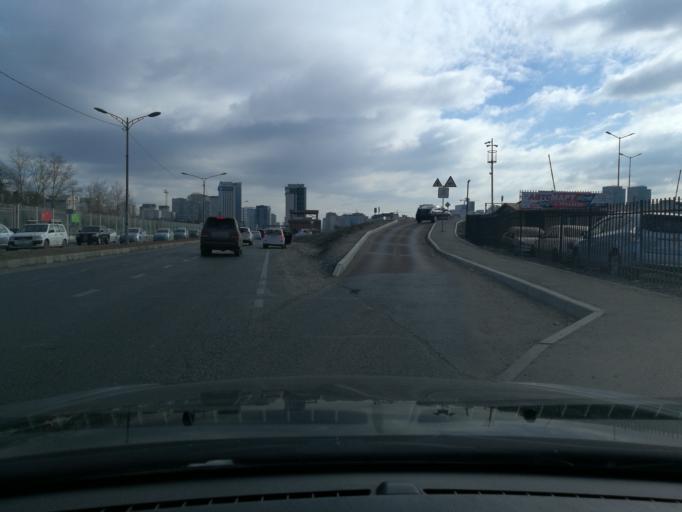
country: MN
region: Ulaanbaatar
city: Ulaanbaatar
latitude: 47.9080
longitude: 106.9175
